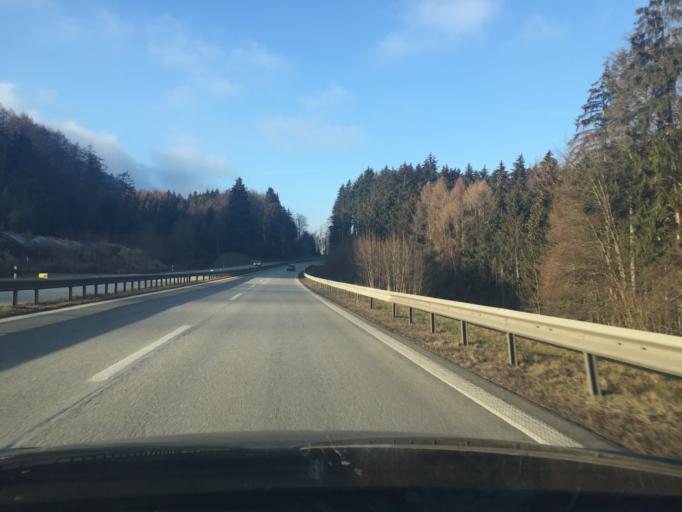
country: DE
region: Bavaria
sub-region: Upper Bavaria
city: Anger
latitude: 47.8103
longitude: 12.8376
